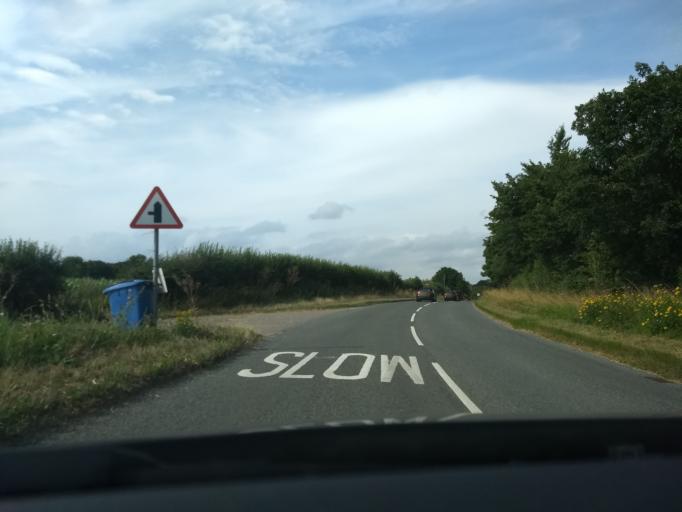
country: GB
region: England
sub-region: Suffolk
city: Ipswich
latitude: 52.0104
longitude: 1.1658
